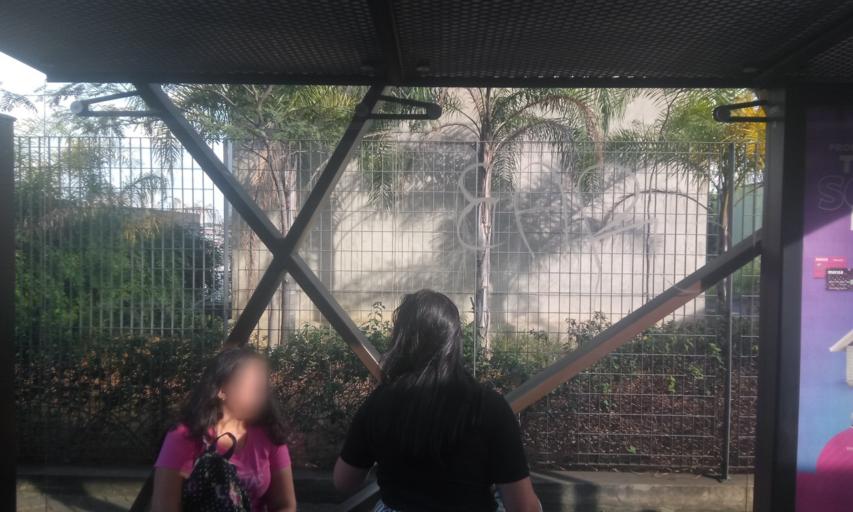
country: BR
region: Sao Paulo
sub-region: Sao Caetano Do Sul
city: Sao Caetano do Sul
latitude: -23.6021
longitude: -46.6074
